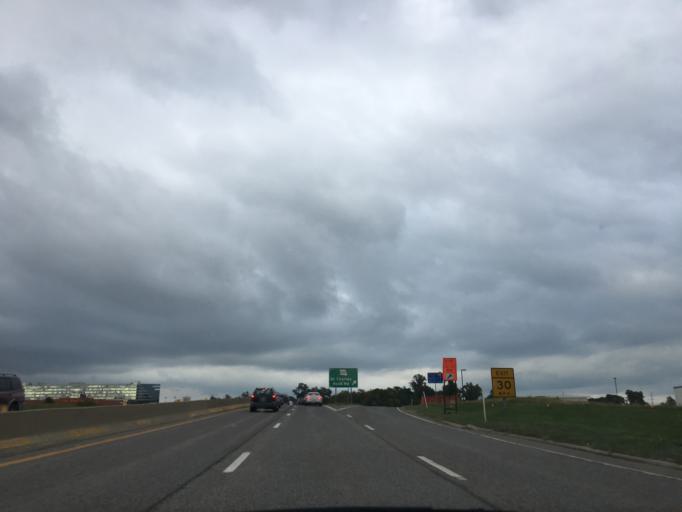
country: US
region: Missouri
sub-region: Saint Louis County
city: Saint Ann
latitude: 38.7361
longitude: -90.4009
